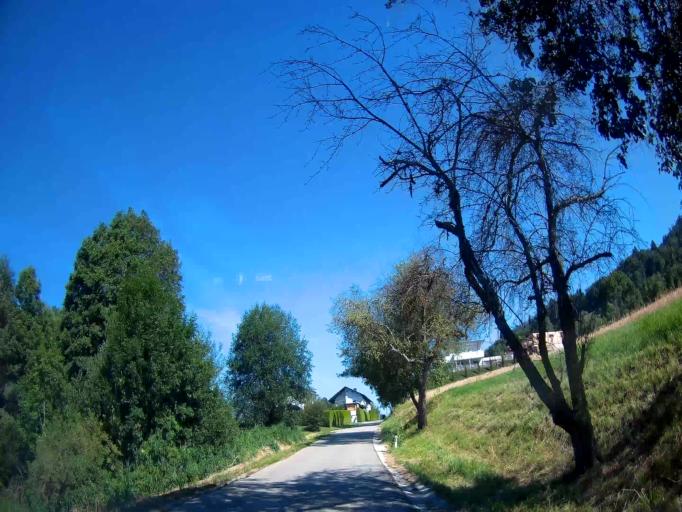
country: AT
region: Carinthia
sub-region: Politischer Bezirk Klagenfurt Land
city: Poggersdorf
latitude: 46.6619
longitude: 14.5375
